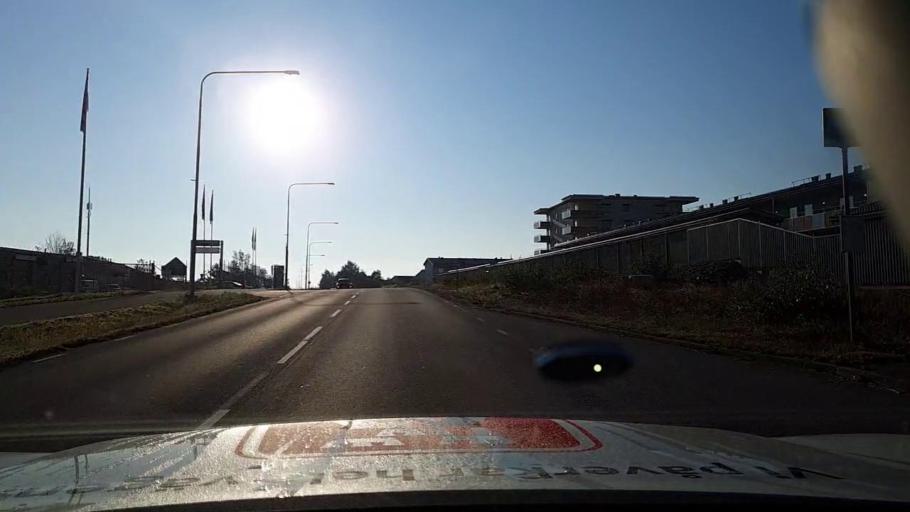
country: SE
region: Kalmar
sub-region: Vasterviks Kommun
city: Vaestervik
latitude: 57.7628
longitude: 16.6010
